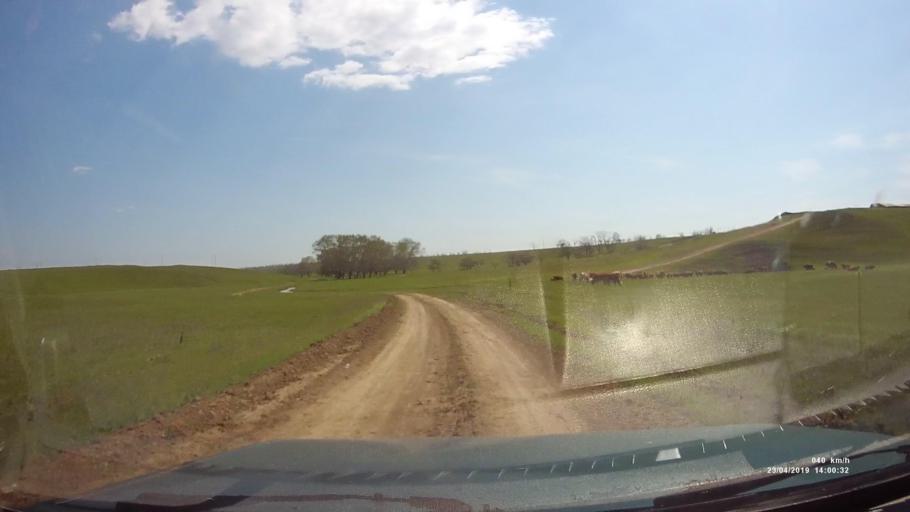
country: RU
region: Rostov
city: Remontnoye
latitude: 46.5589
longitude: 42.9469
